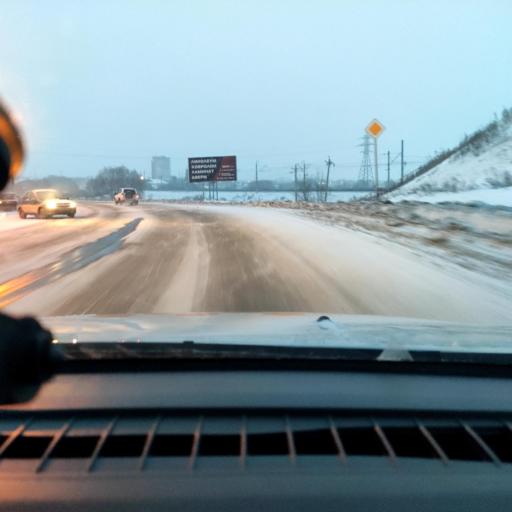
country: RU
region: Samara
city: Kinel'-Cherkassy
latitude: 53.4486
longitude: 51.5115
